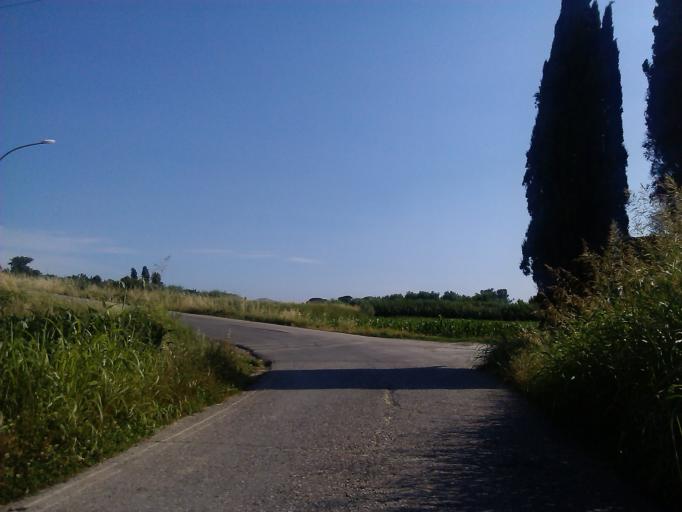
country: IT
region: Tuscany
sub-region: Province of Florence
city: Campi Bisenzio
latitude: 43.8434
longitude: 11.1316
